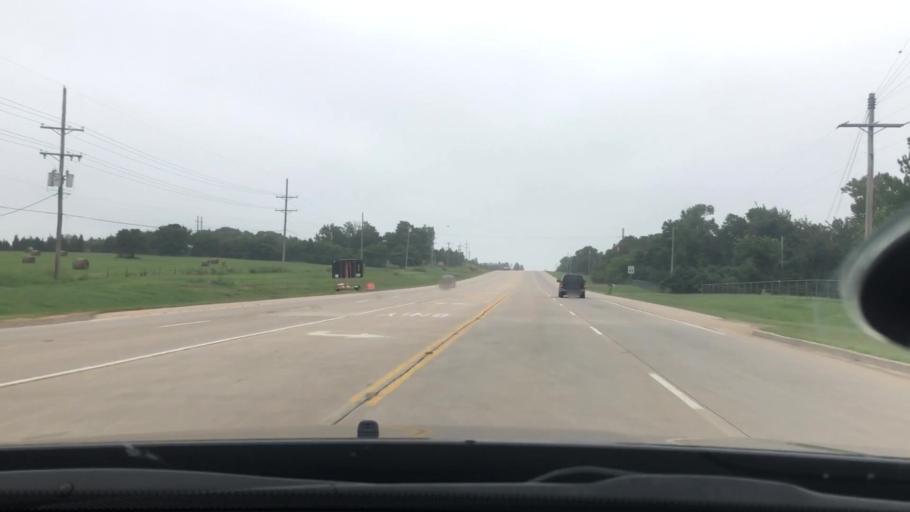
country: US
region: Oklahoma
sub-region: Seminole County
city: Seminole
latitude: 35.2610
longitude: -96.6710
